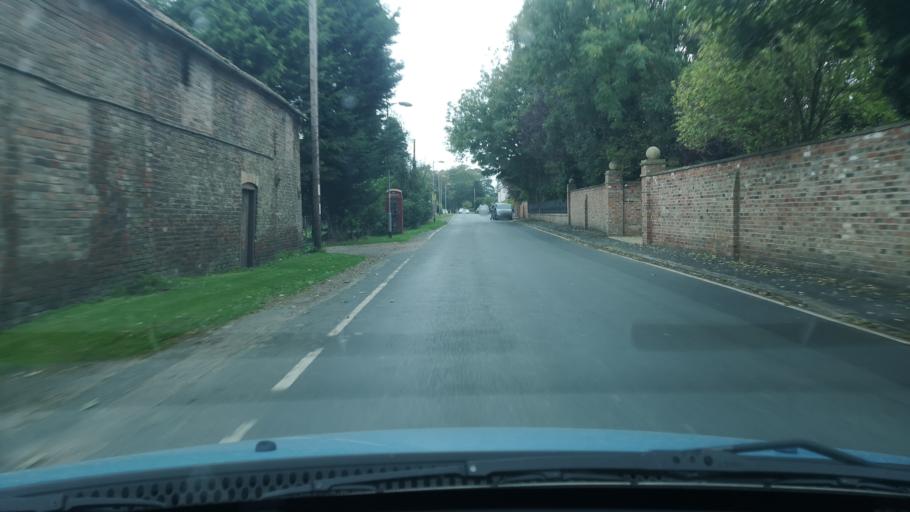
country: GB
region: England
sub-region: East Riding of Yorkshire
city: Laxton
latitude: 53.6988
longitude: -0.7968
